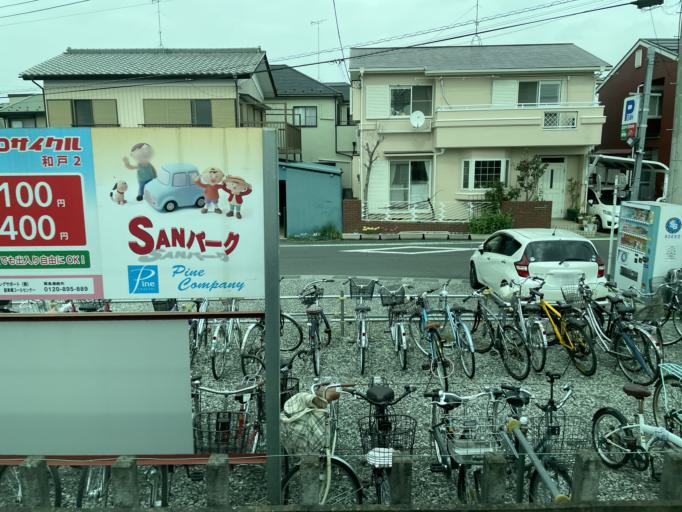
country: JP
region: Saitama
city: Sugito
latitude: 36.0404
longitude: 139.7004
